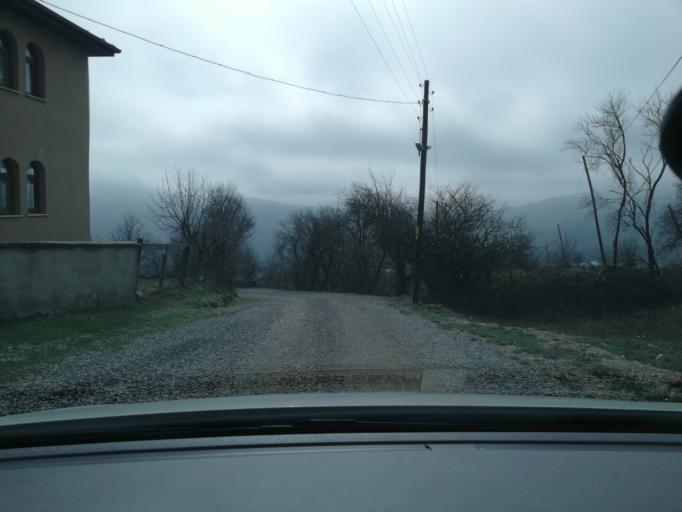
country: TR
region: Bolu
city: Bolu
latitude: 40.6677
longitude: 31.4609
